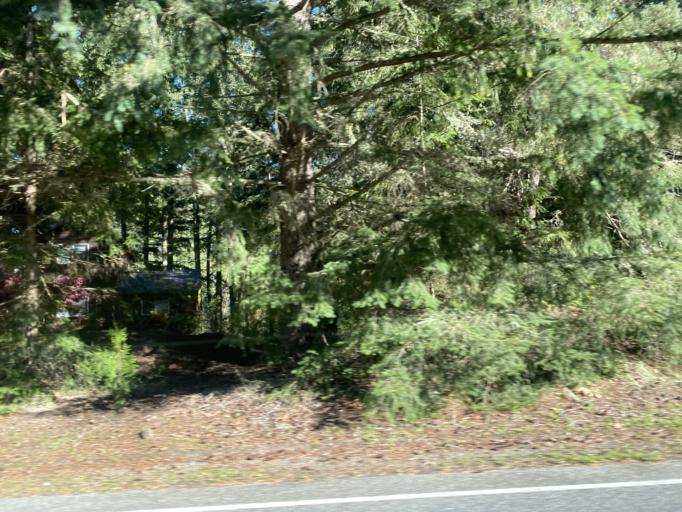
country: US
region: Washington
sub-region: Island County
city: Langley
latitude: 48.0137
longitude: -122.4265
